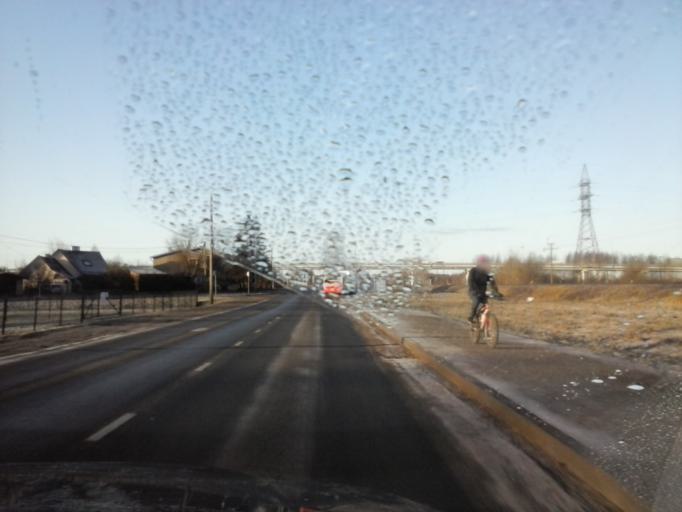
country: EE
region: Tartu
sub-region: Tartu linn
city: Tartu
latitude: 58.3494
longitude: 26.6989
